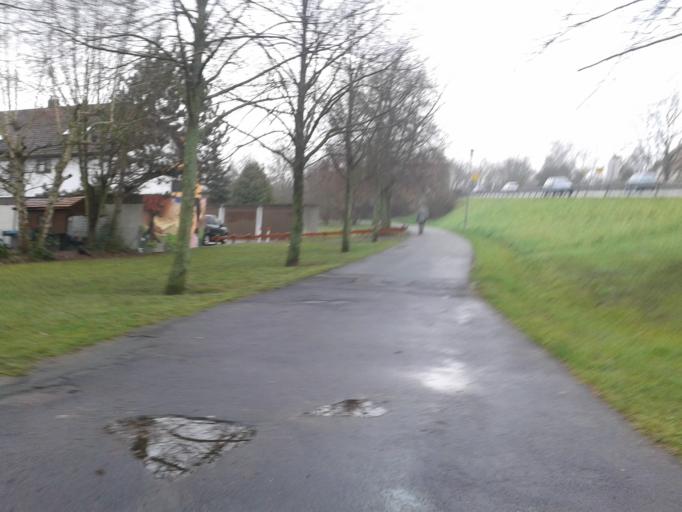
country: DE
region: Bavaria
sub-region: Upper Franconia
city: Hallstadt
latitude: 49.9236
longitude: 10.8747
